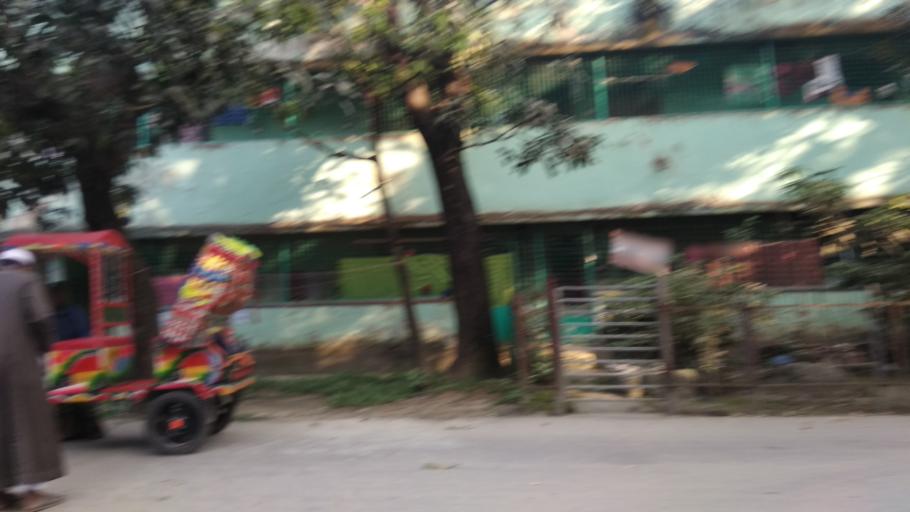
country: BD
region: Dhaka
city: Tungi
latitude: 23.8447
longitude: 90.4180
